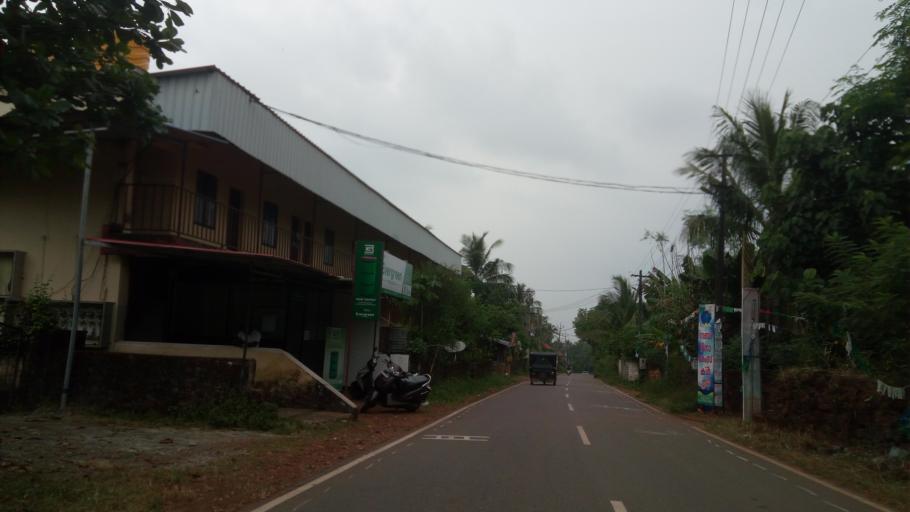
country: IN
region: Kerala
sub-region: Malappuram
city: Malappuram
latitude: 10.9764
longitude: 76.0075
